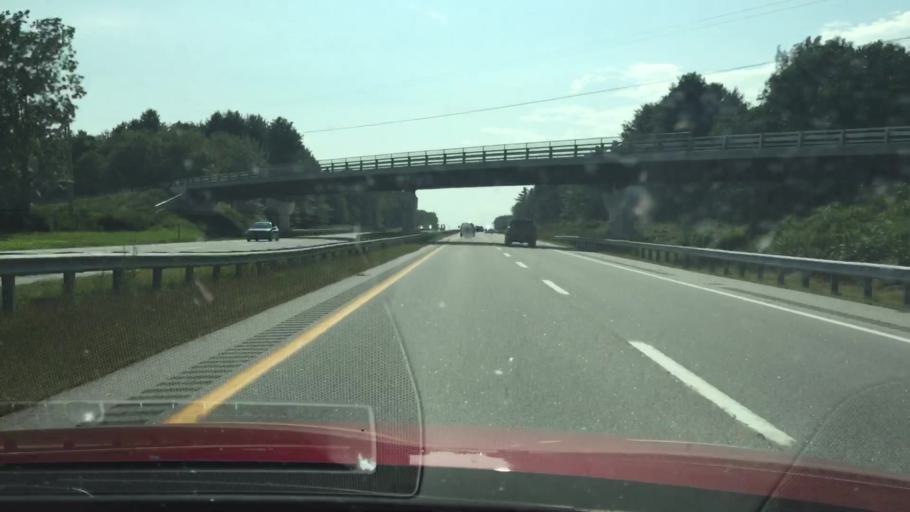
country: US
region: Maine
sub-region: Sagadahoc County
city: Richmond
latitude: 44.1452
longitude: -69.9242
